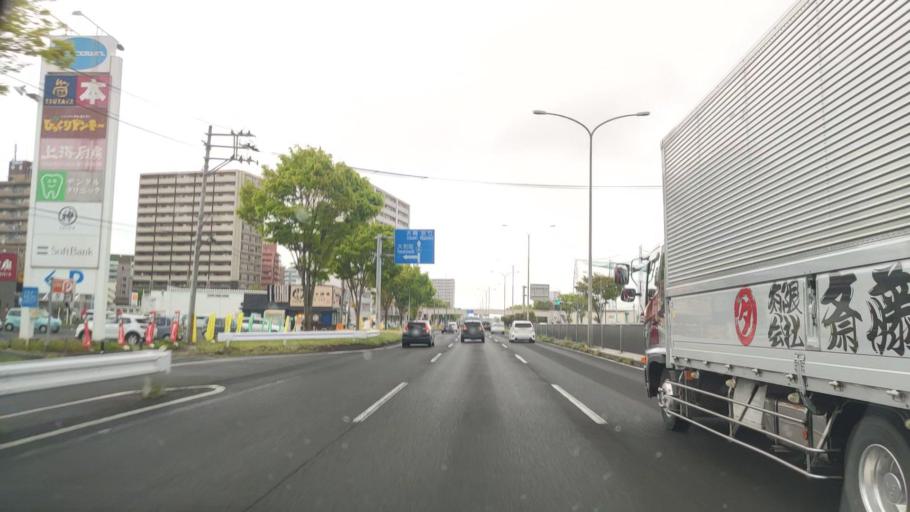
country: JP
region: Miyagi
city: Sendai-shi
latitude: 38.2448
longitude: 140.9229
